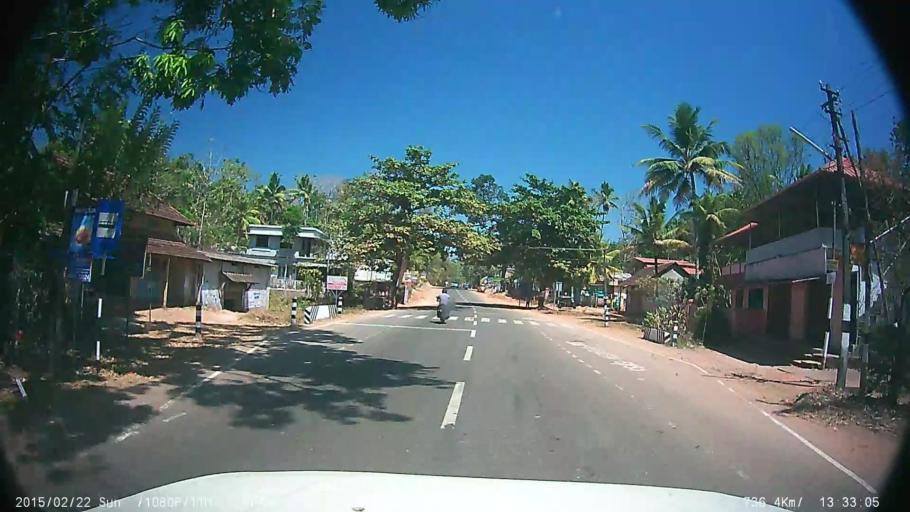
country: IN
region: Kerala
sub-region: Kottayam
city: Changanacheri
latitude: 9.4800
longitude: 76.5891
